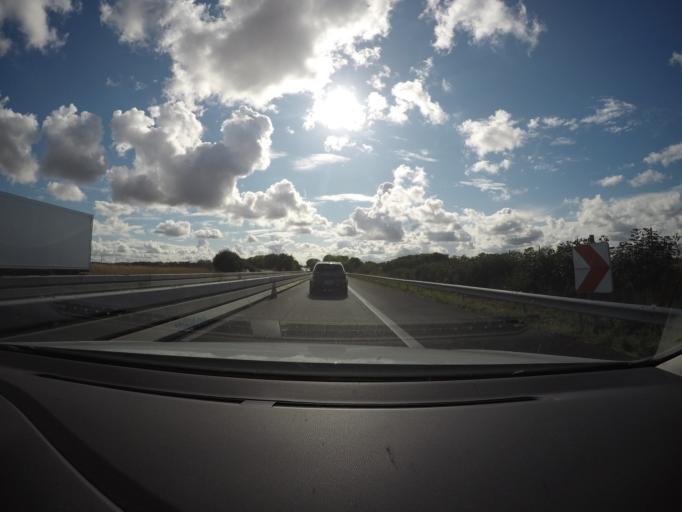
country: FR
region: Nord-Pas-de-Calais
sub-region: Departement du Nord
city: Fontaine-Notre-Dame
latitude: 50.1485
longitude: 3.1347
